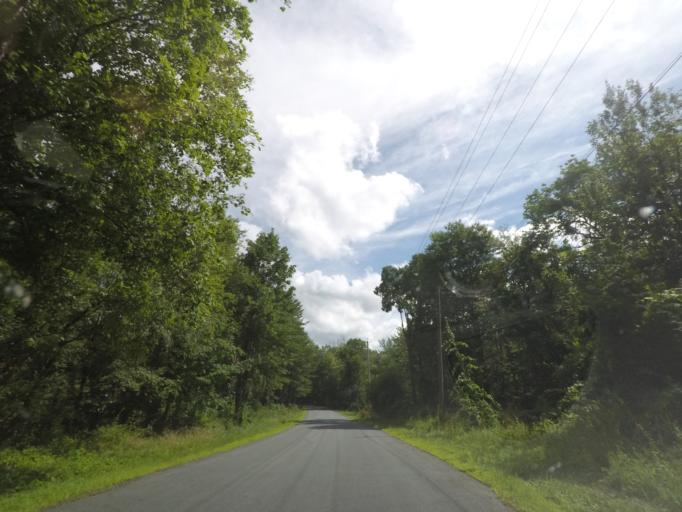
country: US
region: New York
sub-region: Rensselaer County
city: Averill Park
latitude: 42.6614
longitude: -73.5501
